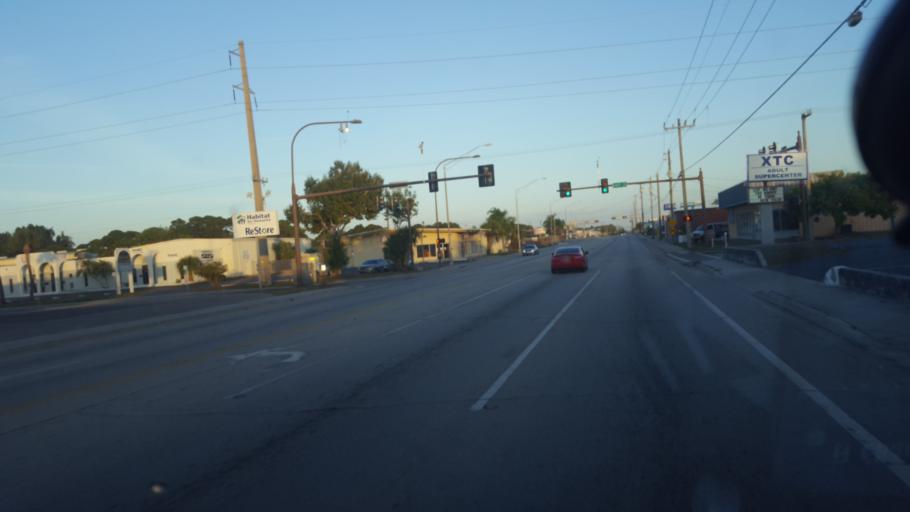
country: US
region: Florida
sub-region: Sarasota County
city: Sarasota
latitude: 27.3522
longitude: -82.5289
